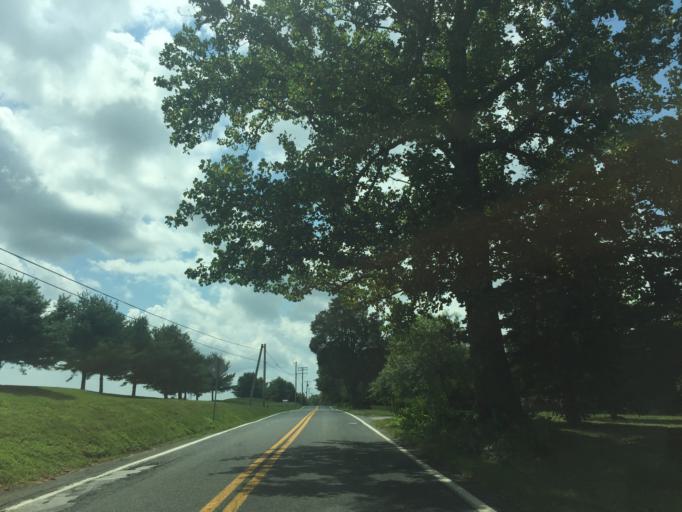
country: US
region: Maryland
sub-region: Baltimore County
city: Kingsville
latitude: 39.4269
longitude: -76.4079
